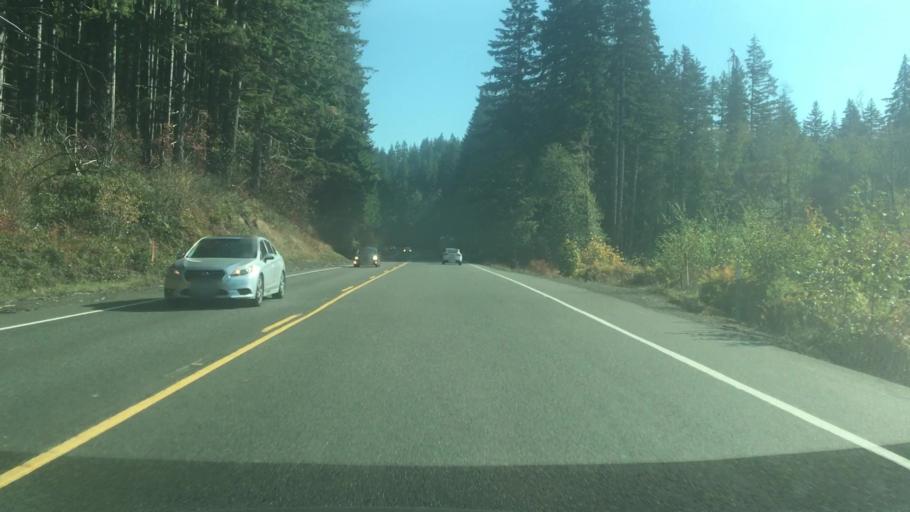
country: US
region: Oregon
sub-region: Polk County
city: Grand Ronde
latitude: 45.0633
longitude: -123.7040
